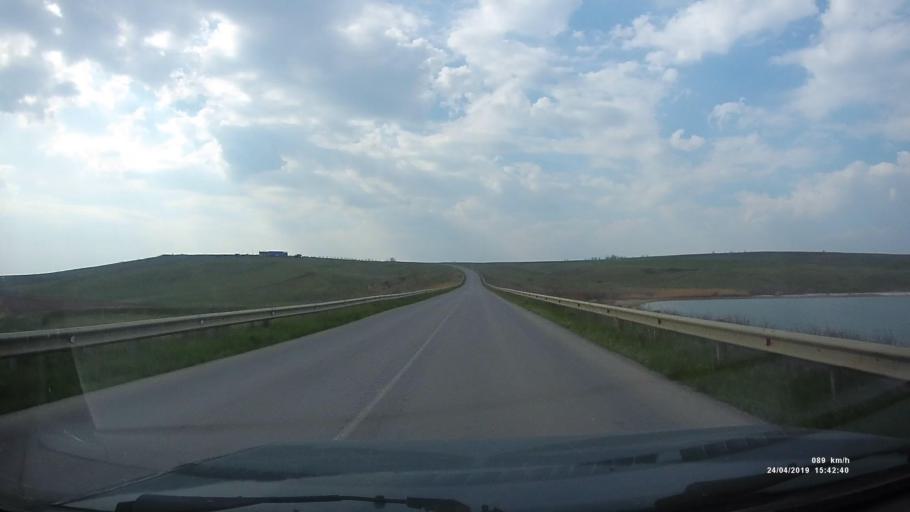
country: RU
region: Kalmykiya
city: Yashalta
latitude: 46.5780
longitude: 42.7849
